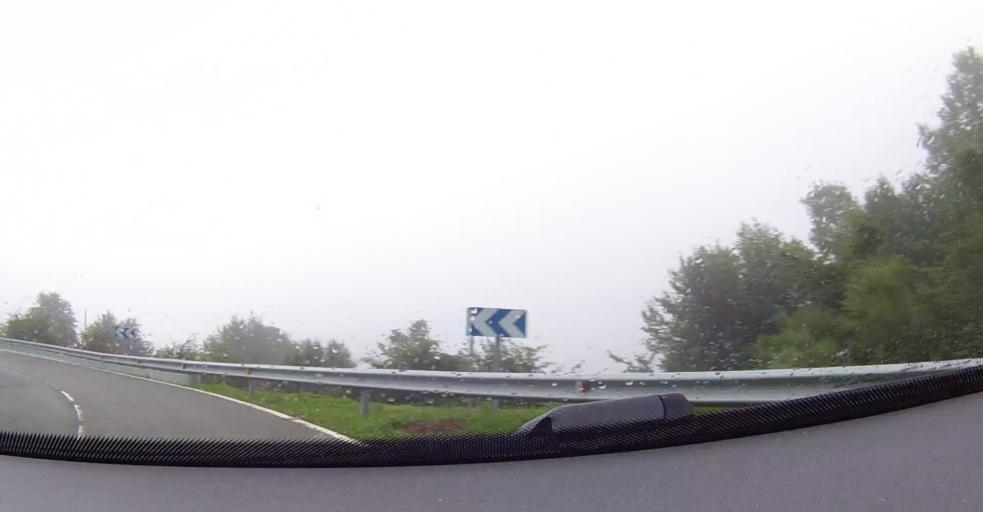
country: ES
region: Cantabria
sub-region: Provincia de Cantabria
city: Camaleno
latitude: 43.0730
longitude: -4.7325
